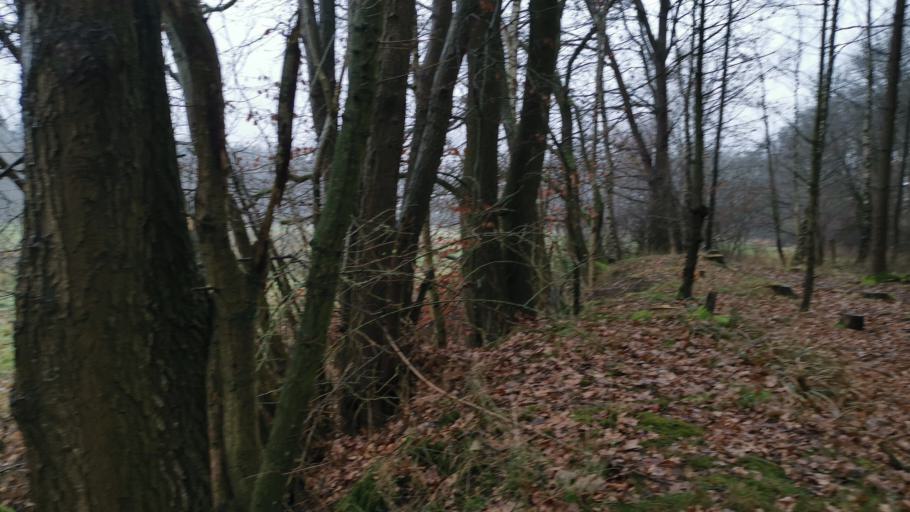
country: DE
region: Schleswig-Holstein
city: Lehmrade
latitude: 53.6049
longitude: 10.7499
